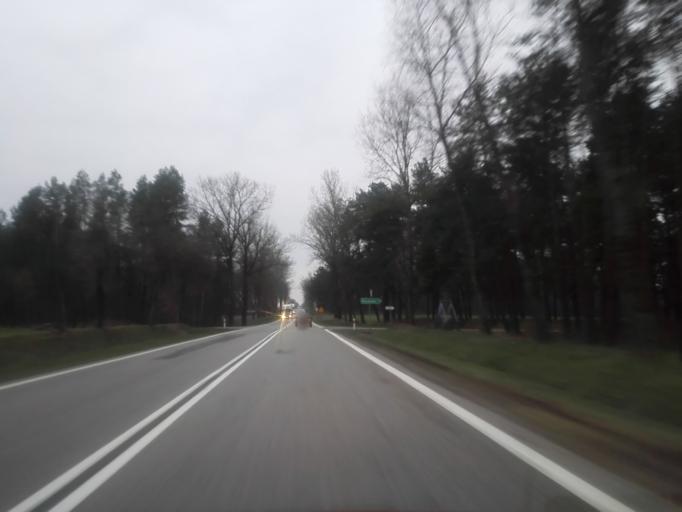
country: PL
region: Podlasie
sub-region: Powiat kolnenski
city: Stawiski
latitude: 53.3117
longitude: 22.1501
